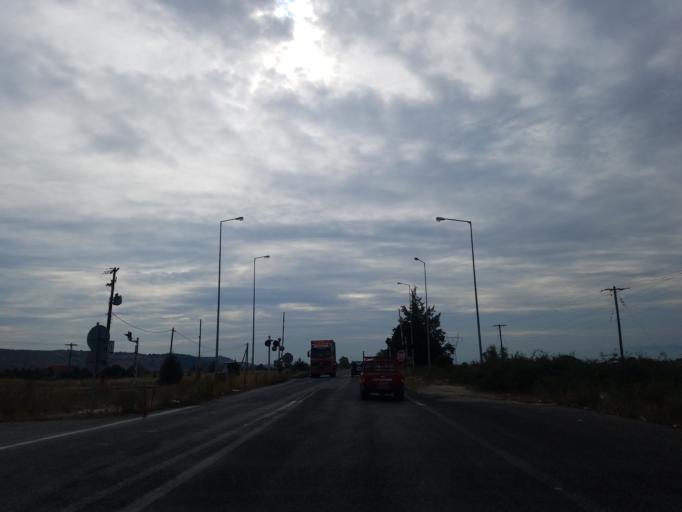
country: GR
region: Thessaly
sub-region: Trikala
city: Vasiliki
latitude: 39.6618
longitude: 21.6736
